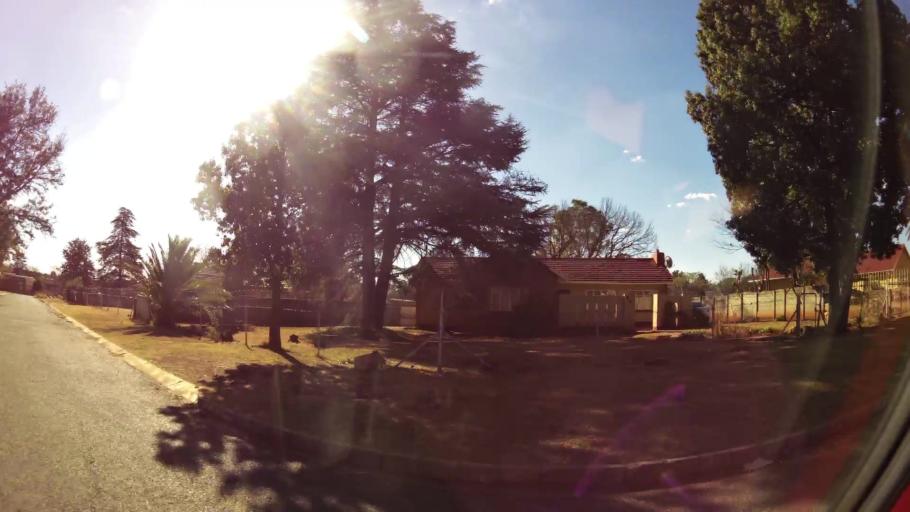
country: ZA
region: Gauteng
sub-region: West Rand District Municipality
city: Carletonville
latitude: -26.3745
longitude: 27.3997
